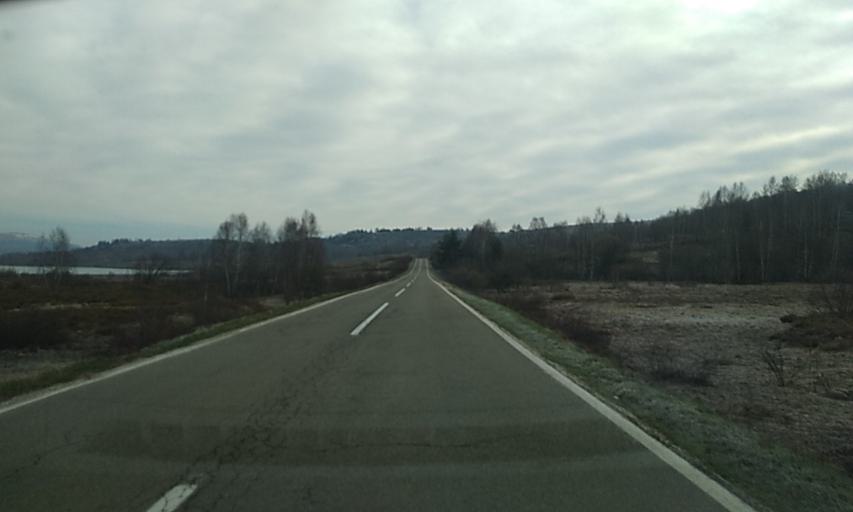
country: RS
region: Central Serbia
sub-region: Jablanicki Okrug
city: Crna Trava
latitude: 42.6732
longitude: 22.3465
